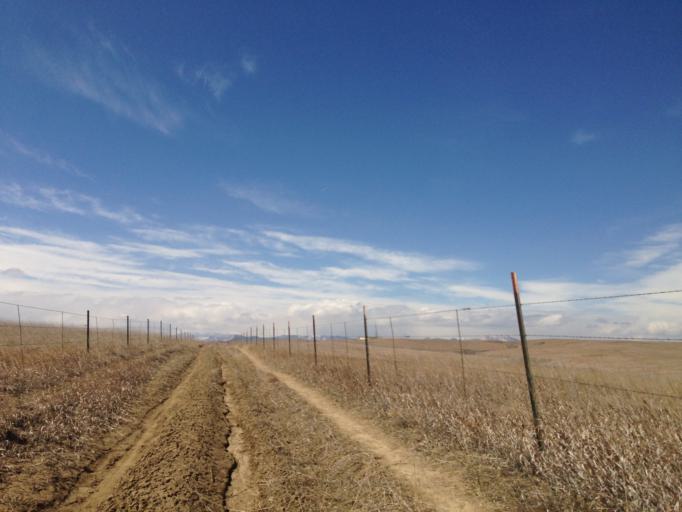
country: US
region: Colorado
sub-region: Boulder County
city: Gunbarrel
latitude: 40.0621
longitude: -105.1413
